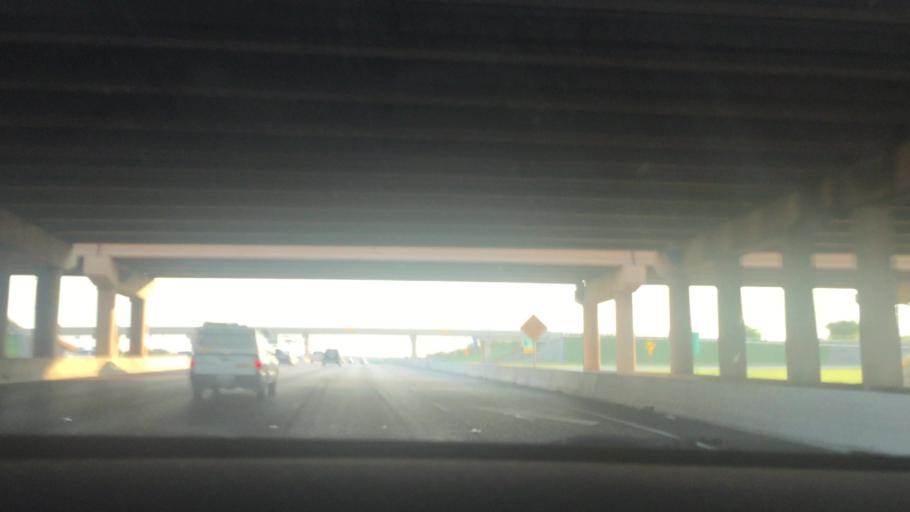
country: US
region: Texas
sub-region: Bexar County
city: Live Oak
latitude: 29.5683
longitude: -98.3330
